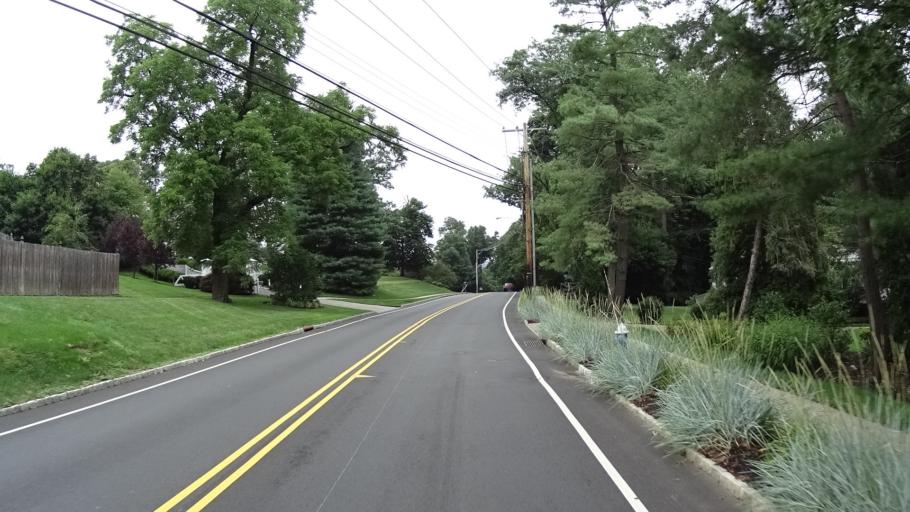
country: US
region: New Jersey
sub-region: Union County
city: New Providence
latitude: 40.6827
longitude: -74.4129
